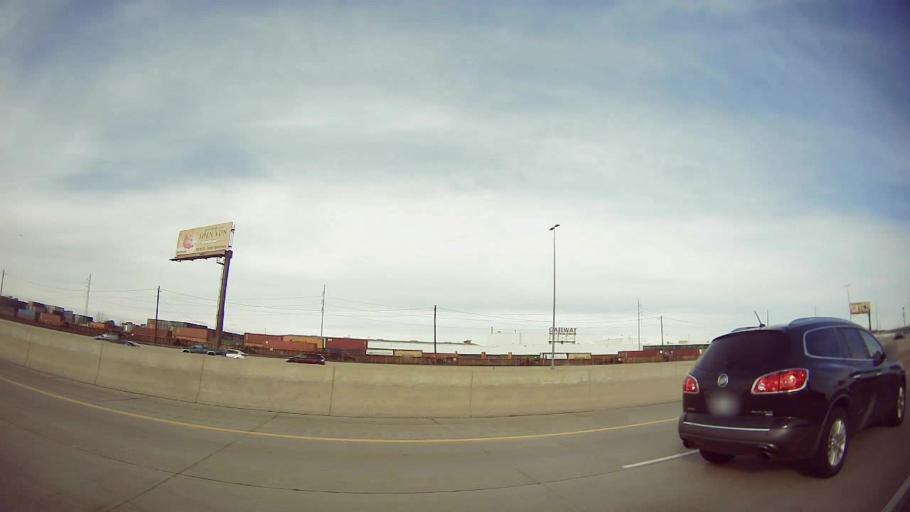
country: US
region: Michigan
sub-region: Wayne County
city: Dearborn Heights
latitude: 42.3780
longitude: -83.2232
